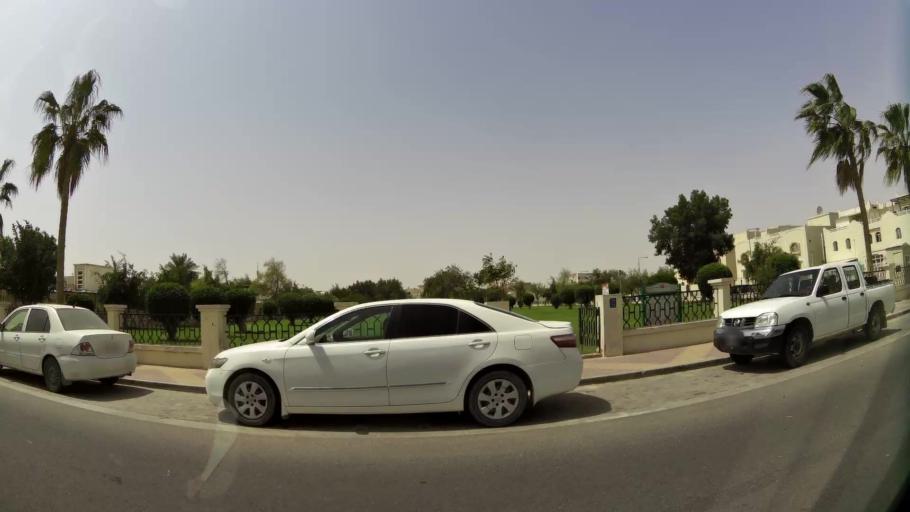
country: QA
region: Baladiyat ad Dawhah
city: Doha
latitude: 25.3182
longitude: 51.4807
